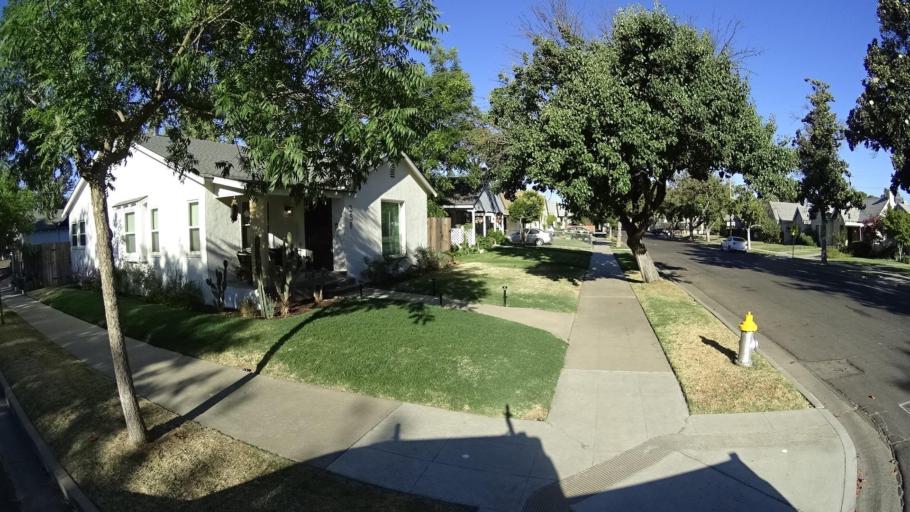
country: US
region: California
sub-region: Fresno County
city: Fresno
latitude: 36.7703
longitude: -119.8075
